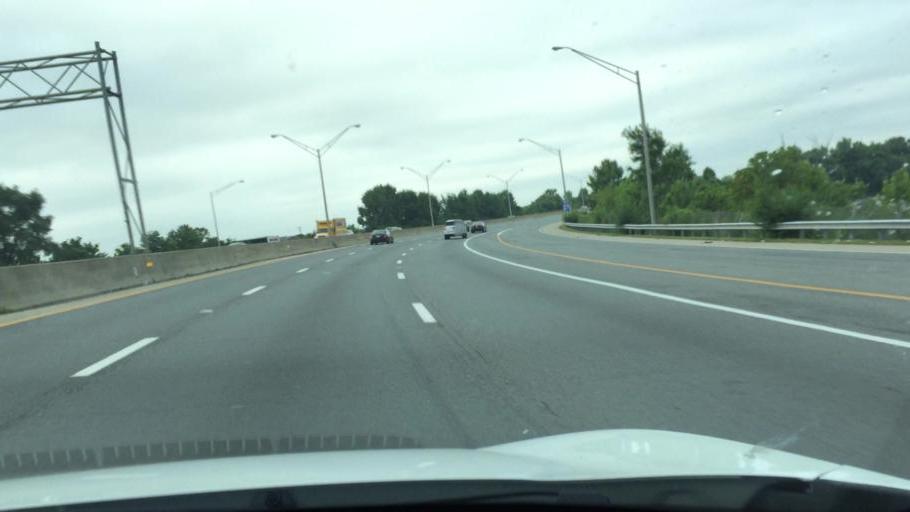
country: US
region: Ohio
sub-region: Franklin County
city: Grandview Heights
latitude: 39.9647
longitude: -83.0298
